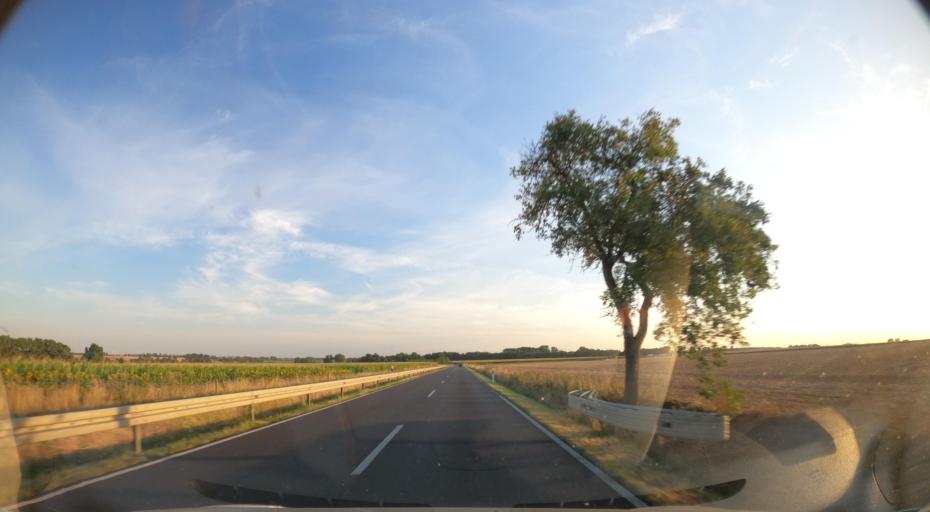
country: DE
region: Mecklenburg-Vorpommern
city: Pasewalk
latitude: 53.5045
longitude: 13.9587
